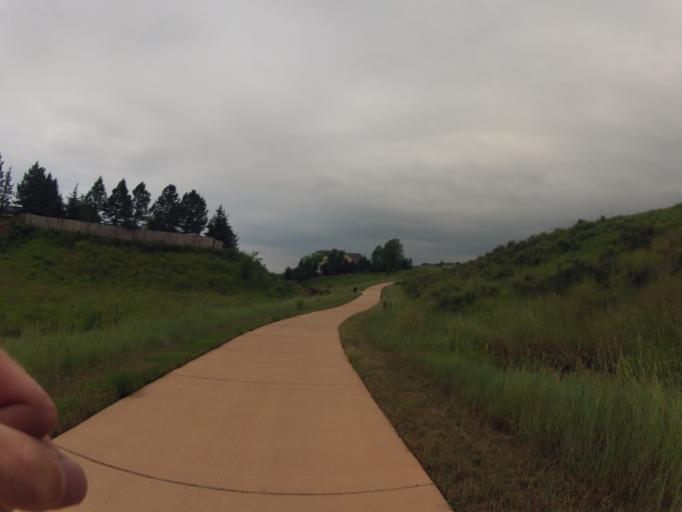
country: US
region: Colorado
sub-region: Larimer County
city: Fort Collins
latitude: 40.5304
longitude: -105.1244
